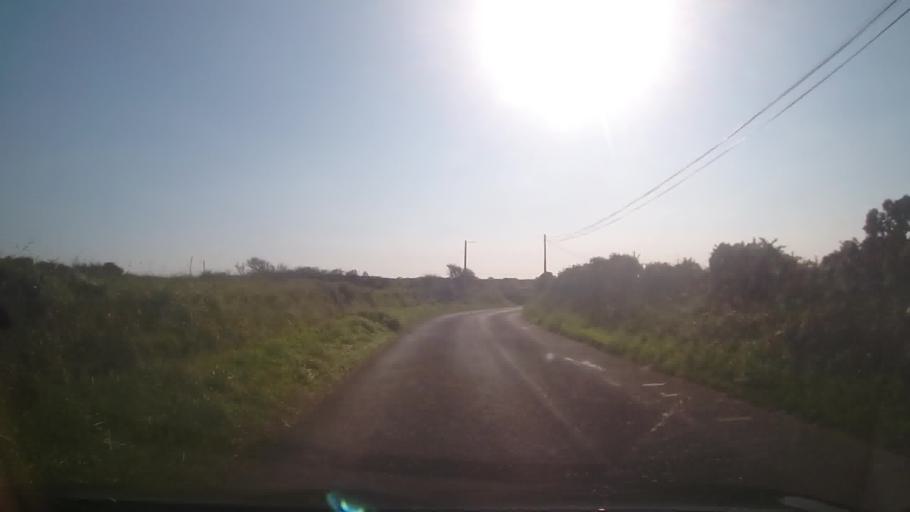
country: GB
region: Wales
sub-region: Pembrokeshire
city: Saint David's
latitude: 51.8917
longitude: -5.2518
